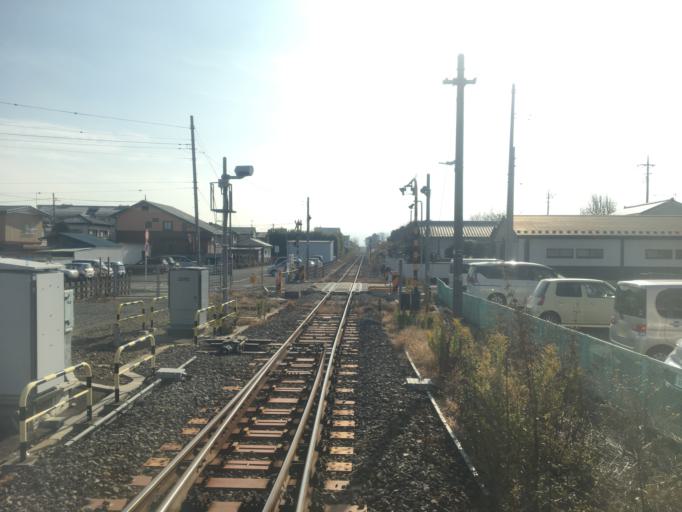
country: JP
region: Gunma
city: Fujioka
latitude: 36.2486
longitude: 139.0834
